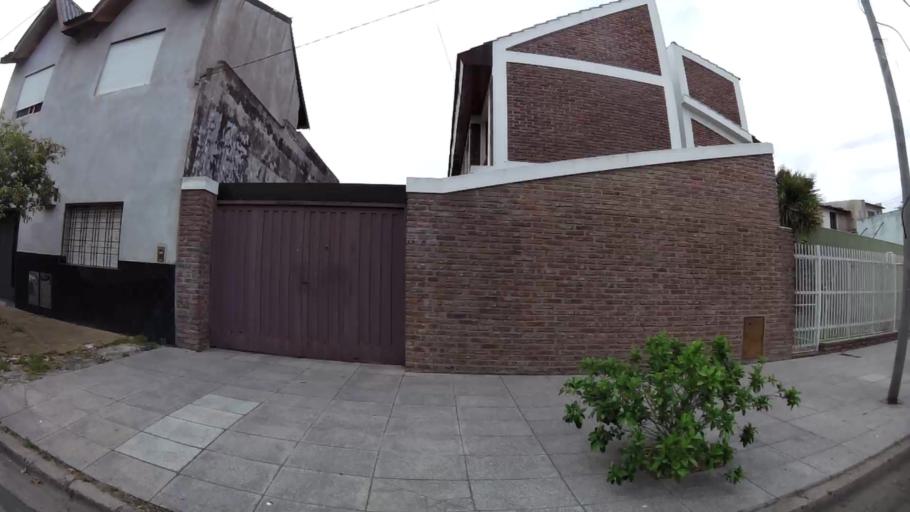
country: AR
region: Buenos Aires F.D.
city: Villa Lugano
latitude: -34.6823
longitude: -58.5075
